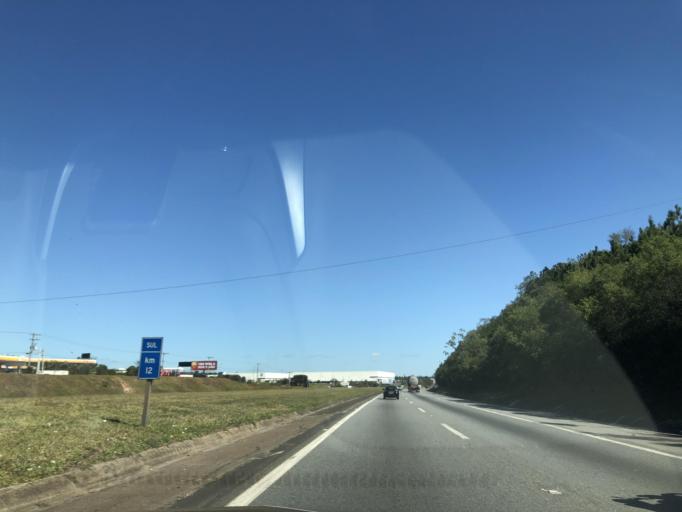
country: BR
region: Sao Paulo
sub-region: Sorocaba
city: Sorocaba
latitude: -23.4139
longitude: -47.3440
